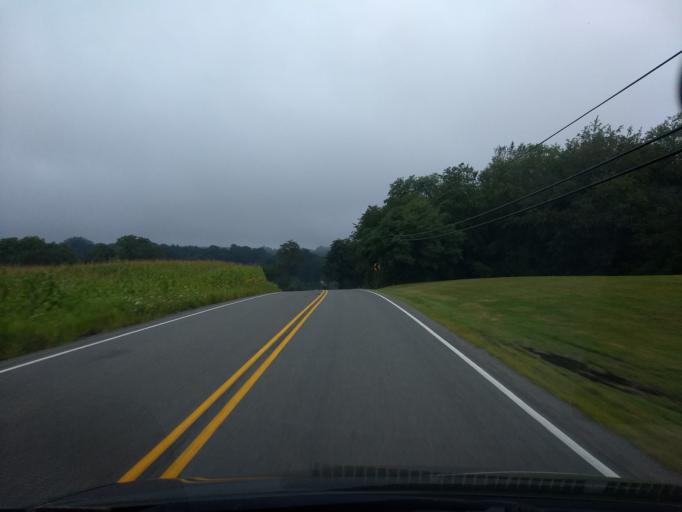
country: US
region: Pennsylvania
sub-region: Westmoreland County
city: Greensburg
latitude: 40.3428
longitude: -79.4979
